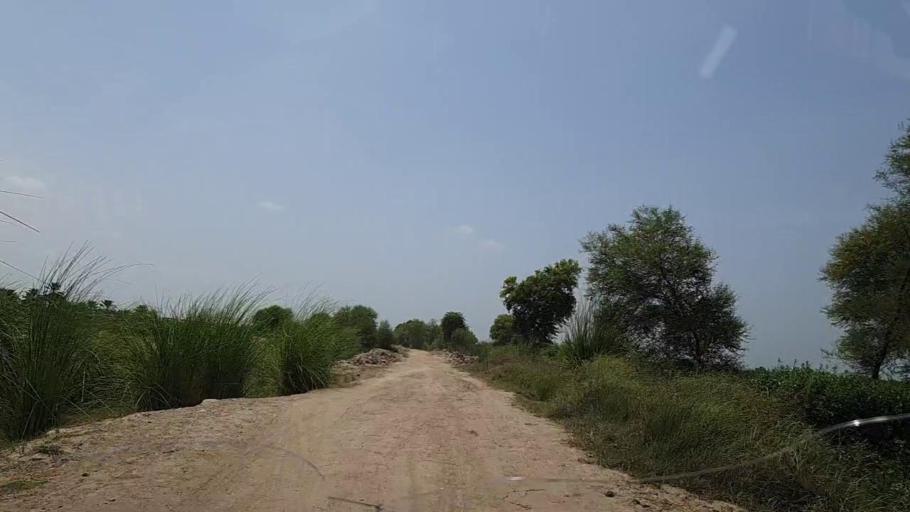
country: PK
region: Sindh
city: Khanpur
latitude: 27.7940
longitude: 69.4593
